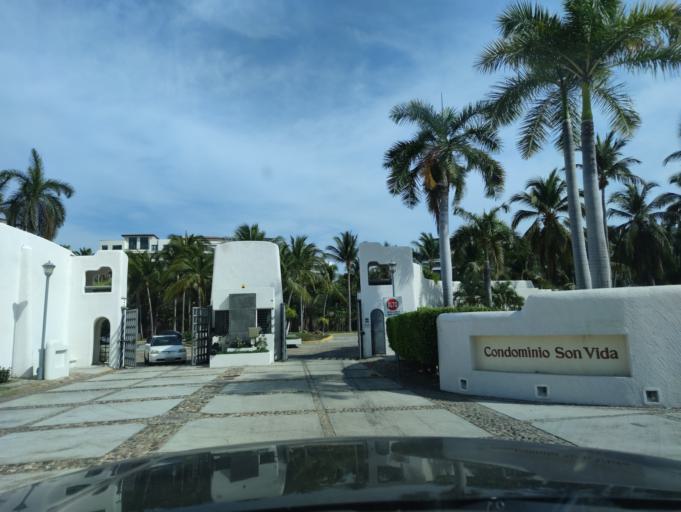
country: MX
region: Guerrero
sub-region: Acapulco de Juarez
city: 10 de Abril
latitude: 16.7701
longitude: -99.7793
